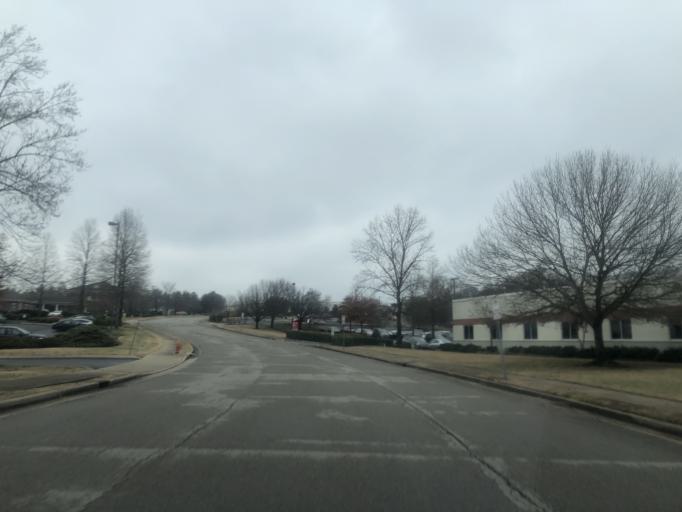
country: US
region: Tennessee
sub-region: Davidson County
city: Lakewood
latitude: 36.1447
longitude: -86.6743
